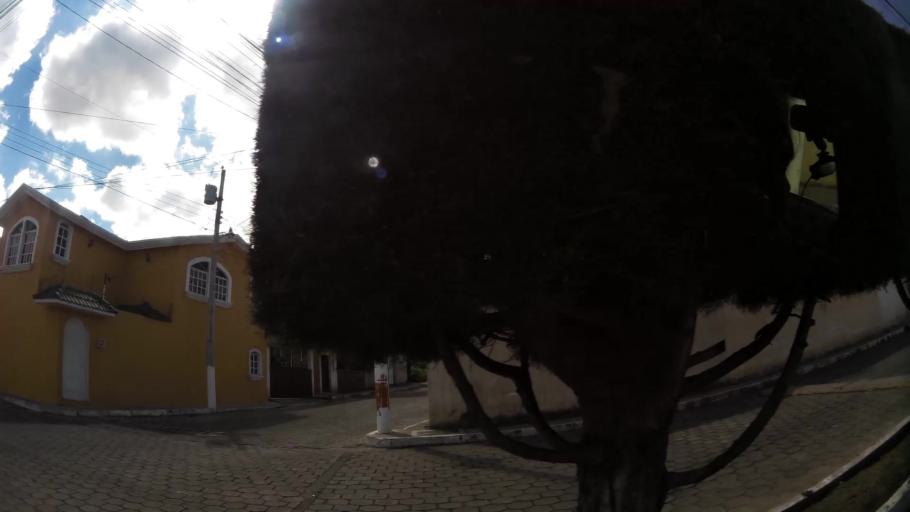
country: GT
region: Quetzaltenango
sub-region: Municipio de La Esperanza
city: La Esperanza
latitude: 14.8510
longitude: -91.5423
